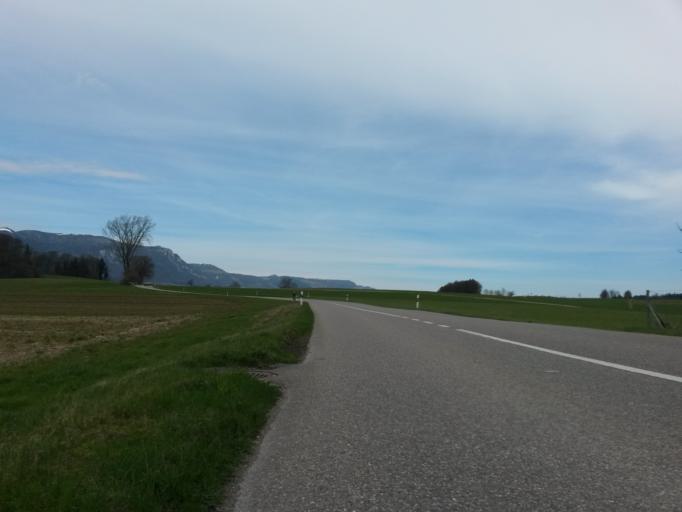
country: CH
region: Bern
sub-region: Seeland District
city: Leuzigen
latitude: 47.1810
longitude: 7.4795
